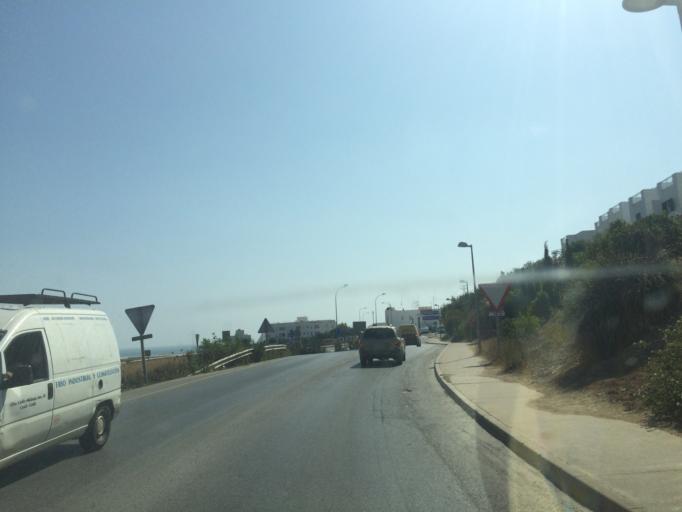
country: ES
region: Andalusia
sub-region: Provincia de Cadiz
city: Conil de la Frontera
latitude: 36.2773
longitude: -6.0792
